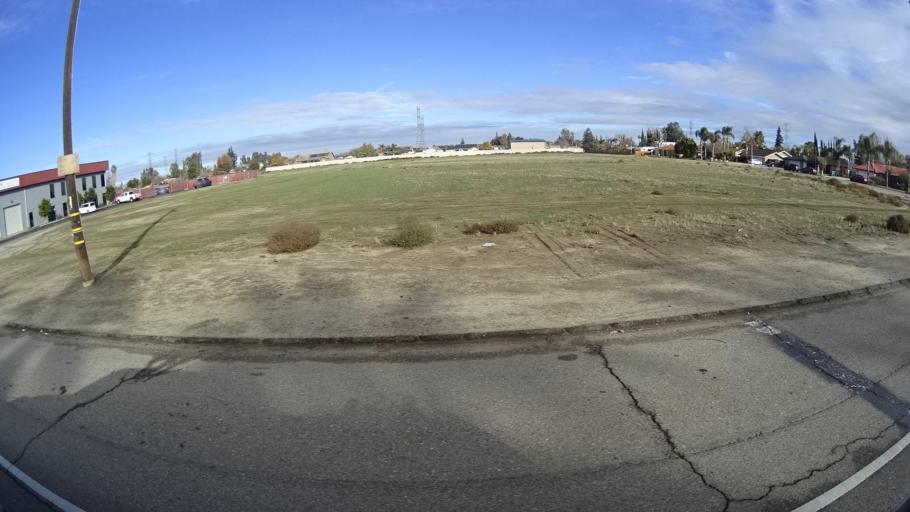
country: US
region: California
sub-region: Kern County
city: Rosedale
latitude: 35.3834
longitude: -119.1395
